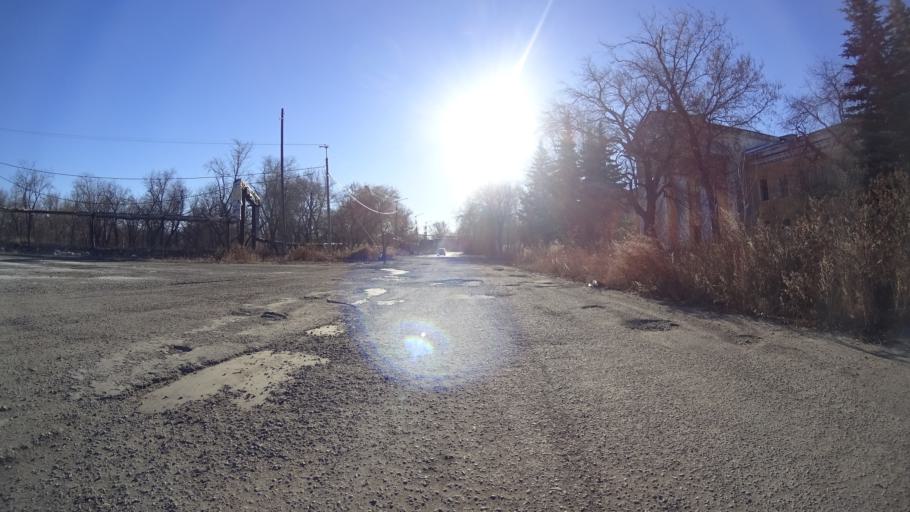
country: RU
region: Chelyabinsk
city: Troitsk
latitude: 54.1025
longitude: 61.5551
